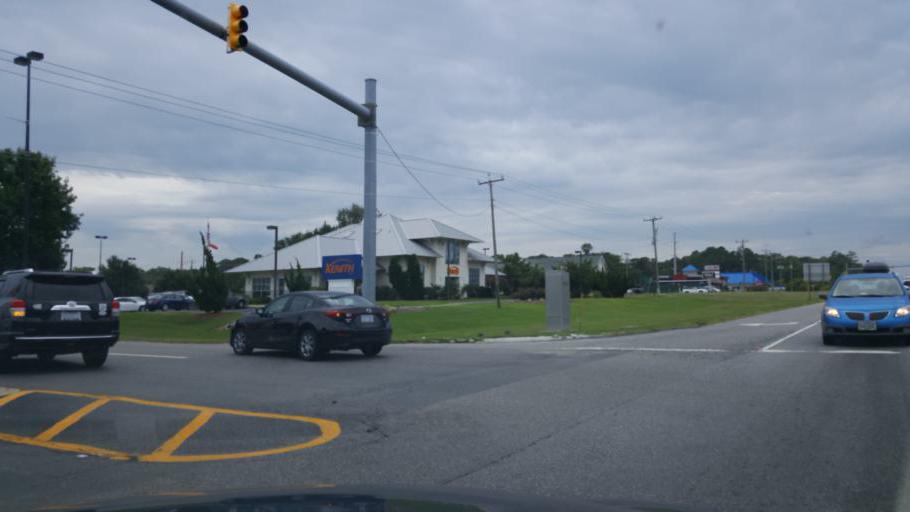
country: US
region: North Carolina
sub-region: Dare County
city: Kitty Hawk
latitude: 36.0990
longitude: -75.7203
